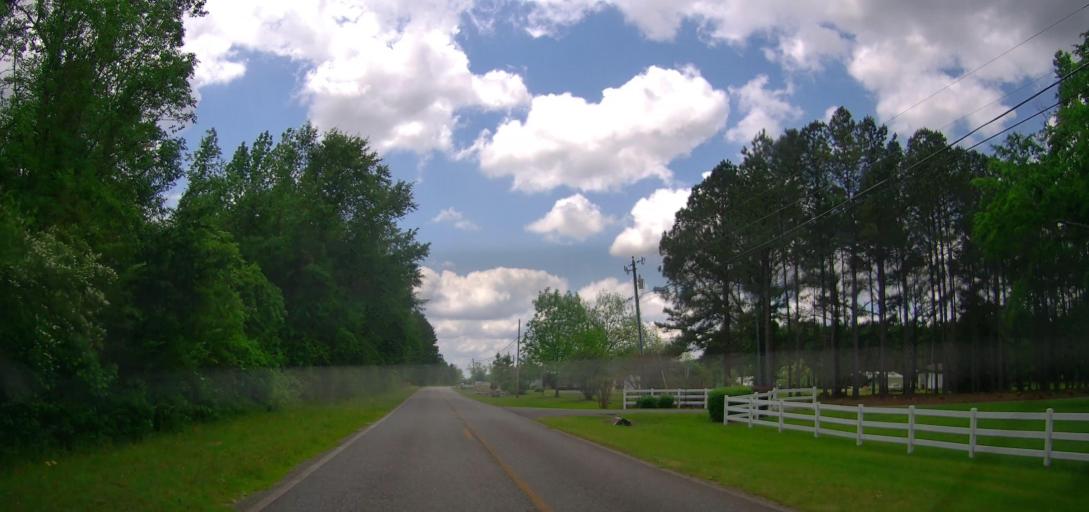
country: US
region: Georgia
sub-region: Laurens County
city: Dublin
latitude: 32.6045
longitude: -82.9482
